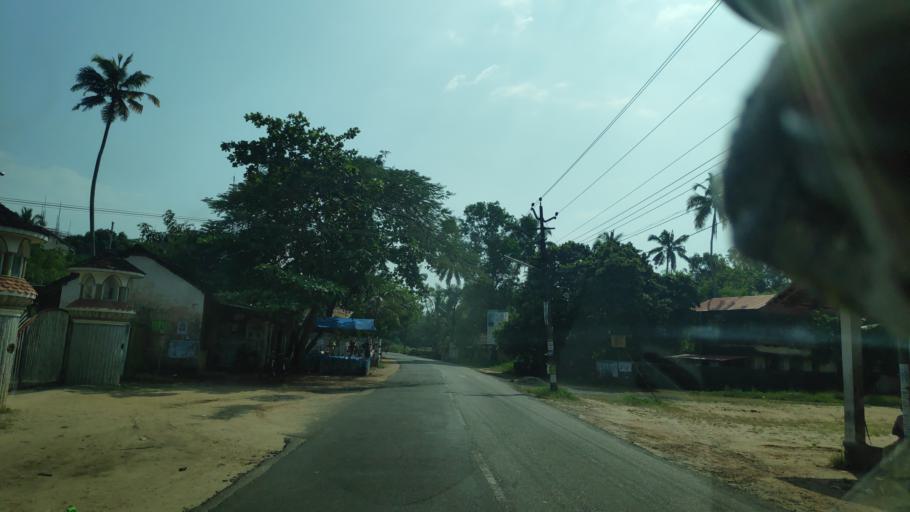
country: IN
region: Kerala
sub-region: Alappuzha
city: Shertallai
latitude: 9.6220
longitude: 76.3006
